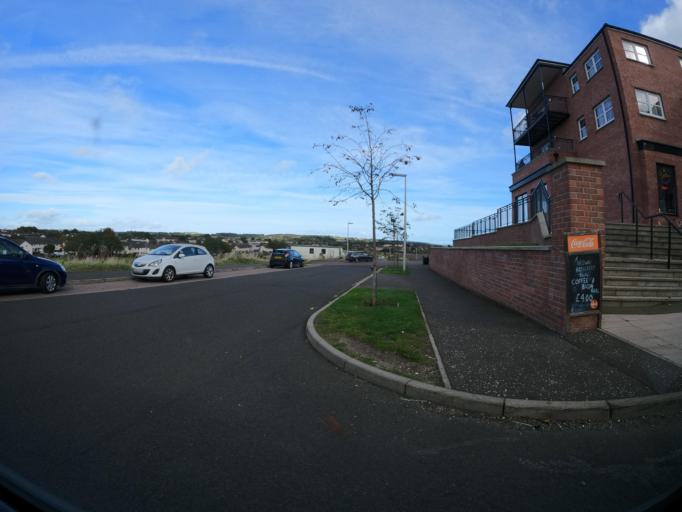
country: GB
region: Scotland
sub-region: Fife
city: Rosyth
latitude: 56.0380
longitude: -3.4381
